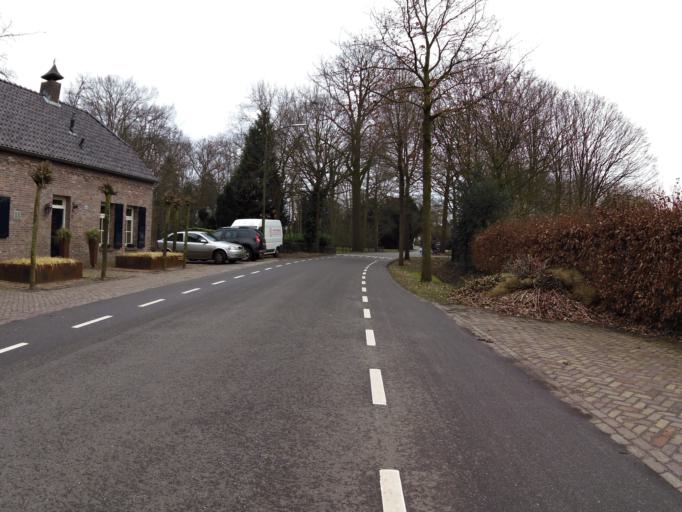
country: NL
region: North Brabant
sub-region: Gemeente Sint-Michielsgestel
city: Sint-Michielsgestel
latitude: 51.6558
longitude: 5.3466
